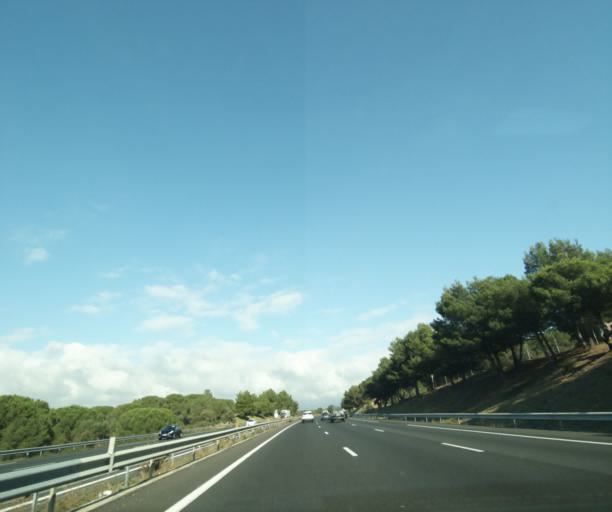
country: FR
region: Languedoc-Roussillon
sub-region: Departement de l'Aude
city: Vinassan
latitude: 43.2234
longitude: 3.0969
